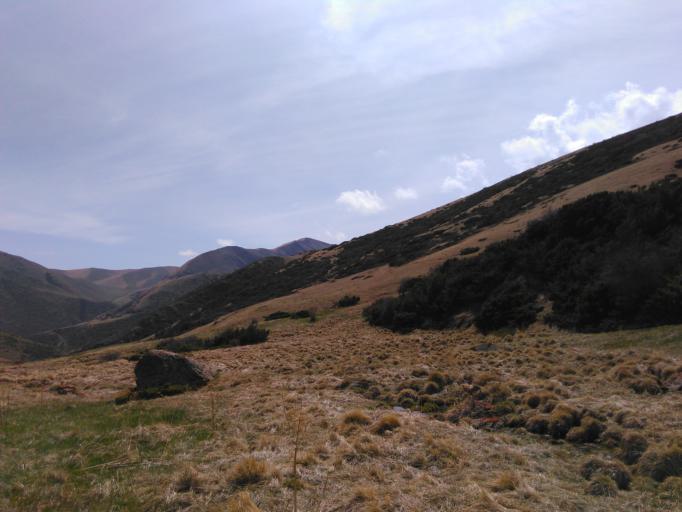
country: KG
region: Chuy
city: Bystrovka
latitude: 42.5162
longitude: 75.6310
